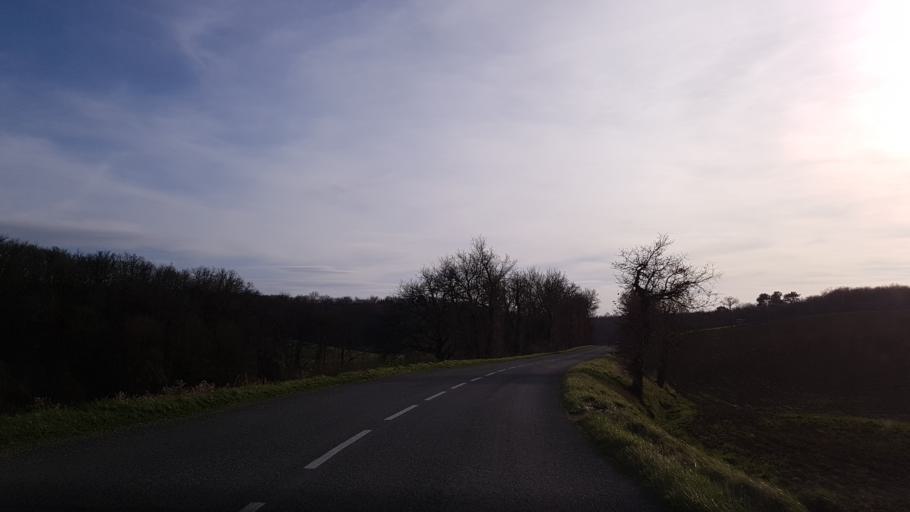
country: FR
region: Languedoc-Roussillon
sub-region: Departement de l'Aude
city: Villeneuve-la-Comptal
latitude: 43.2225
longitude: 1.9178
